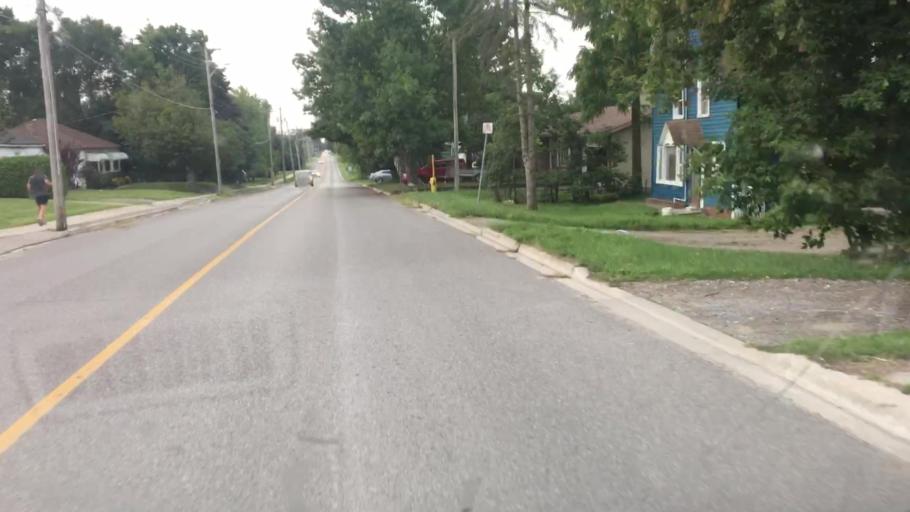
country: CA
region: Ontario
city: Quinte West
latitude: 44.0394
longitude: -77.7464
